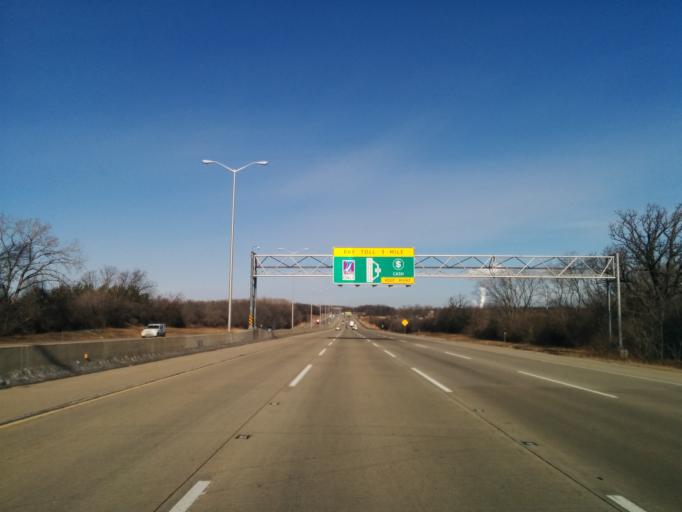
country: US
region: Illinois
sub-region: Lake County
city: Wadsworth
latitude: 42.4139
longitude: -87.9479
